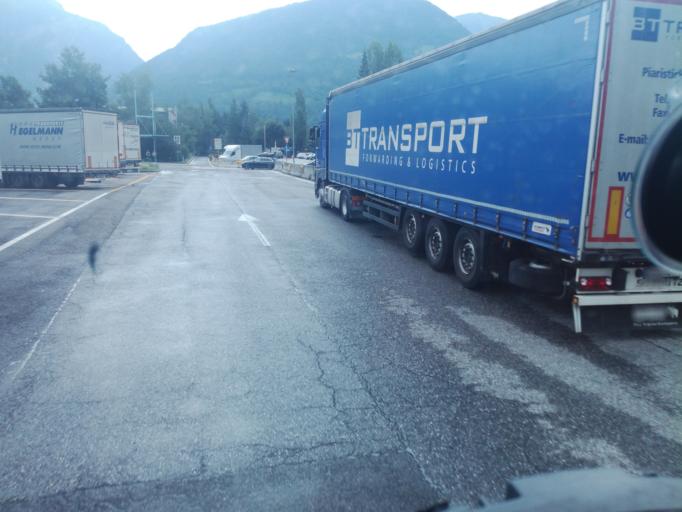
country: IT
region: Trentino-Alto Adige
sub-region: Bolzano
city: Vipiteno
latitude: 46.8800
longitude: 11.4367
